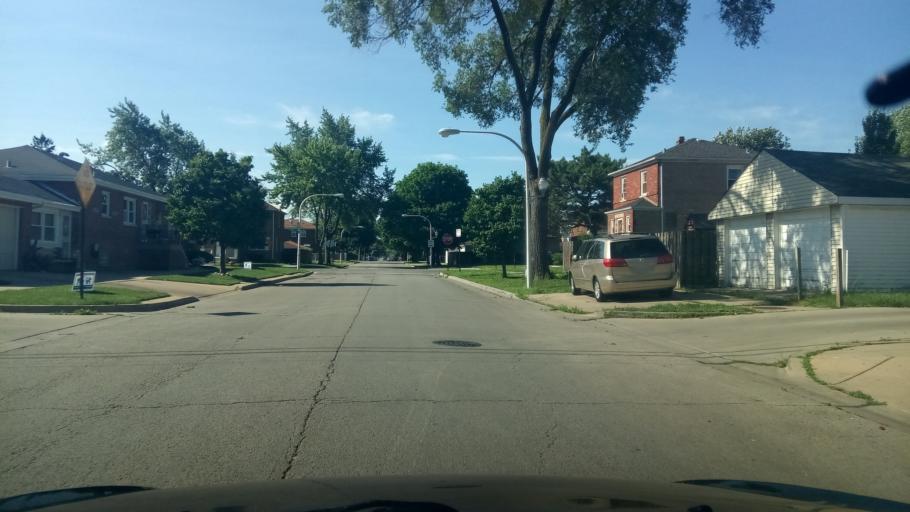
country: US
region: Illinois
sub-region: Cook County
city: Hometown
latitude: 41.7706
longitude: -87.7153
